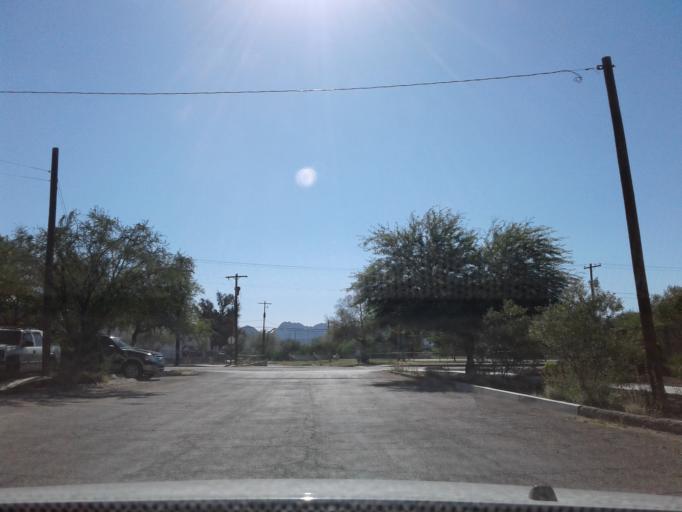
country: US
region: Arizona
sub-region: Pima County
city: South Tucson
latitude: 32.2342
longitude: -110.9773
